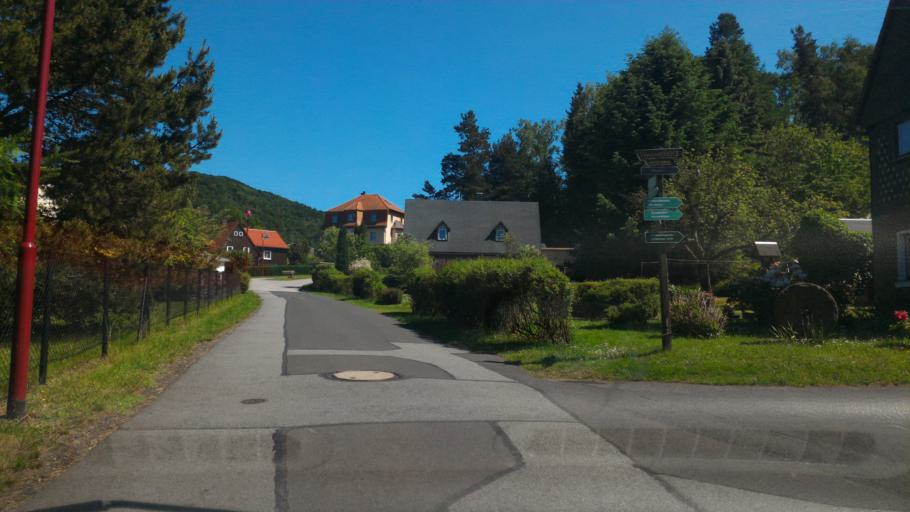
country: DE
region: Saxony
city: Kurort Jonsdorf
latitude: 50.8525
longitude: 14.6996
